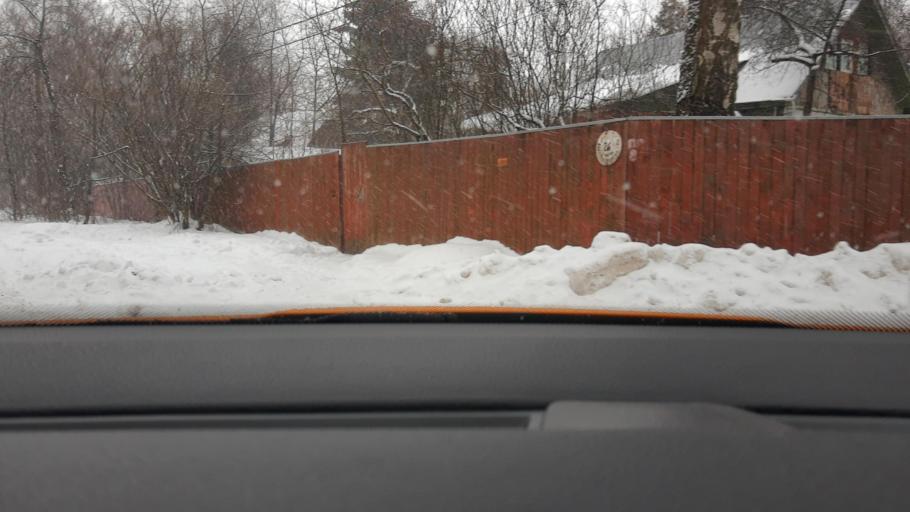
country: RU
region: Moscow
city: Mikhalkovo
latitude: 55.6694
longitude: 37.4236
